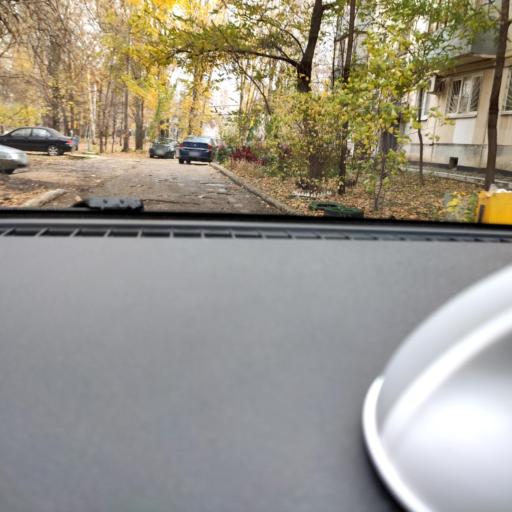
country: RU
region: Samara
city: Samara
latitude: 53.2425
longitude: 50.2167
